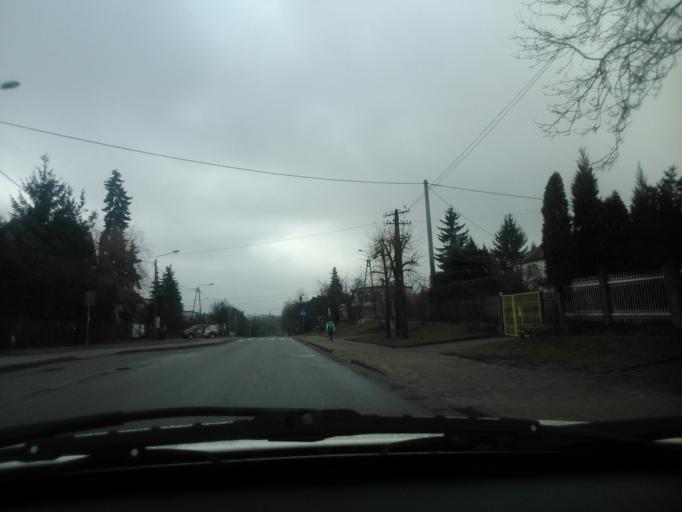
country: PL
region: Kujawsko-Pomorskie
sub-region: Powiat brodnicki
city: Brodnica
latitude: 53.2684
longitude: 19.4068
